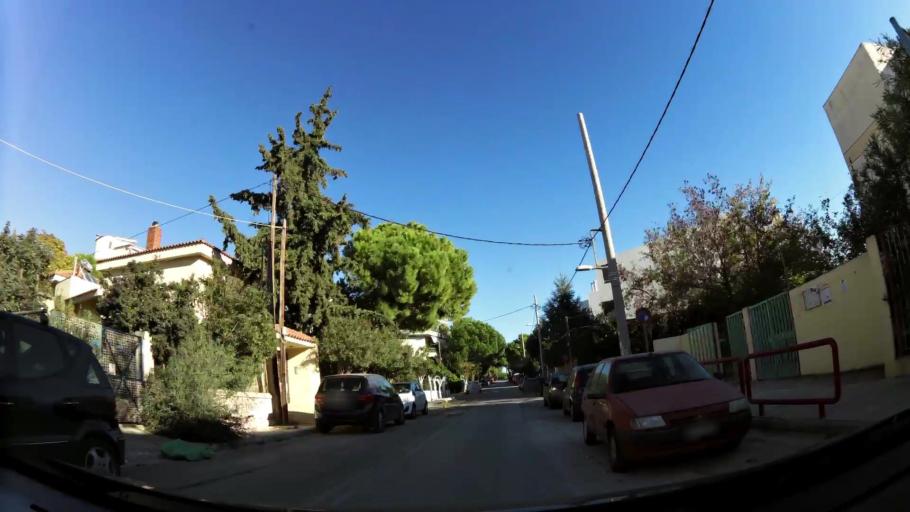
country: GR
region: Attica
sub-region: Nomarchia Athinas
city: Melissia
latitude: 38.0444
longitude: 23.8456
